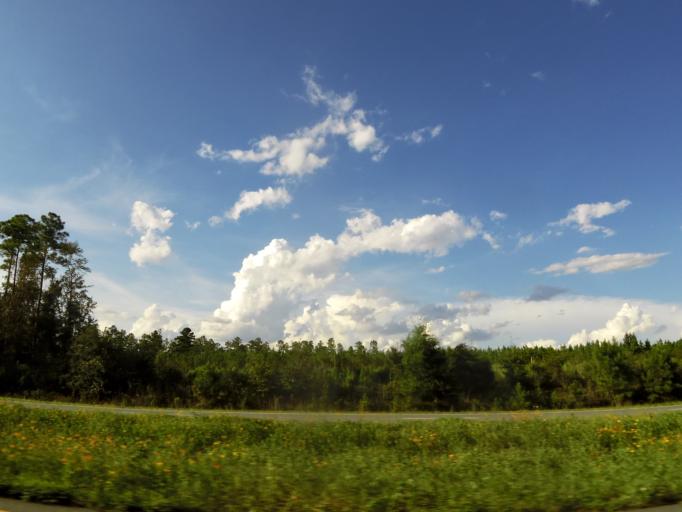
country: US
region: Georgia
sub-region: Brooks County
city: Quitman
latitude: 30.7948
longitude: -83.4348
